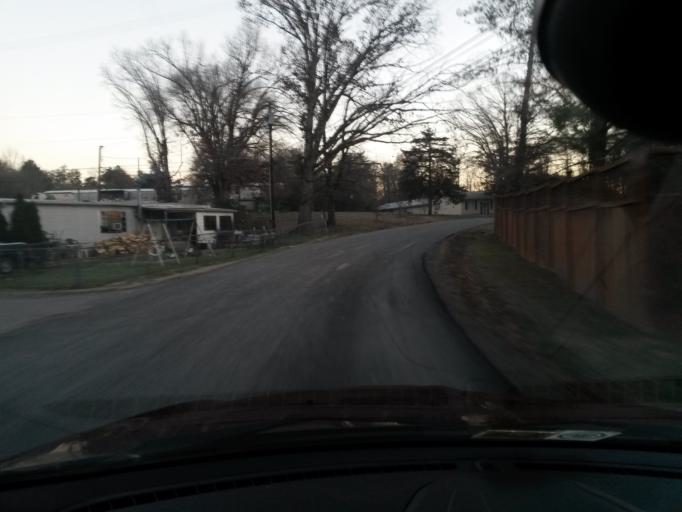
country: US
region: Virginia
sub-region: Alleghany County
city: Clifton Forge
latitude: 37.8235
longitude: -79.7987
